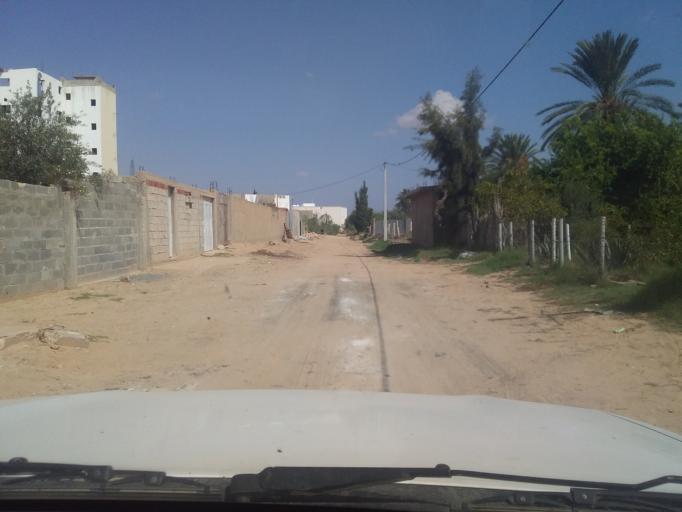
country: TN
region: Qabis
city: Gabes
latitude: 33.6263
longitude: 10.2824
